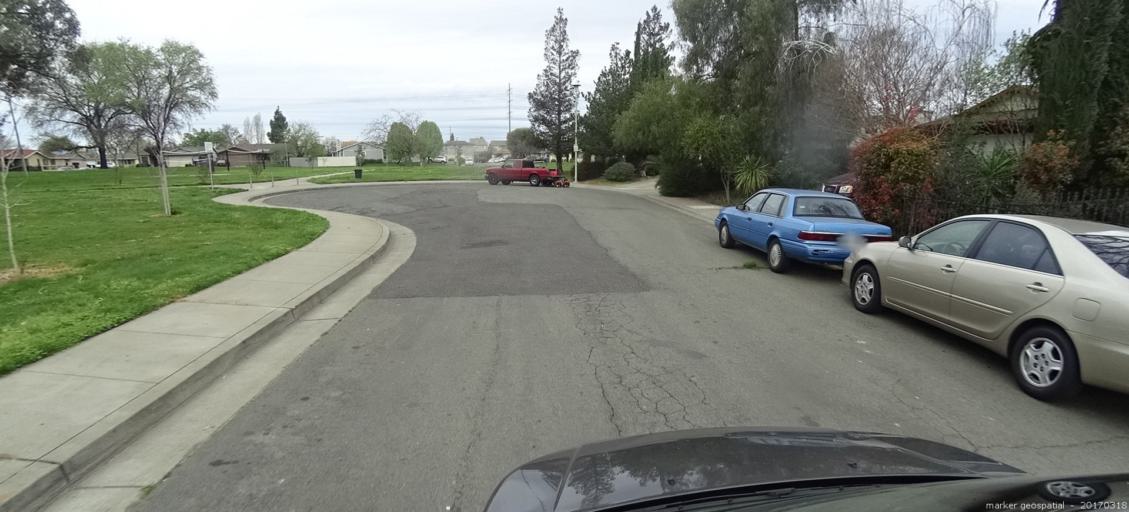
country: US
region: California
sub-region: Sacramento County
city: Parkway
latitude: 38.4863
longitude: -121.4648
